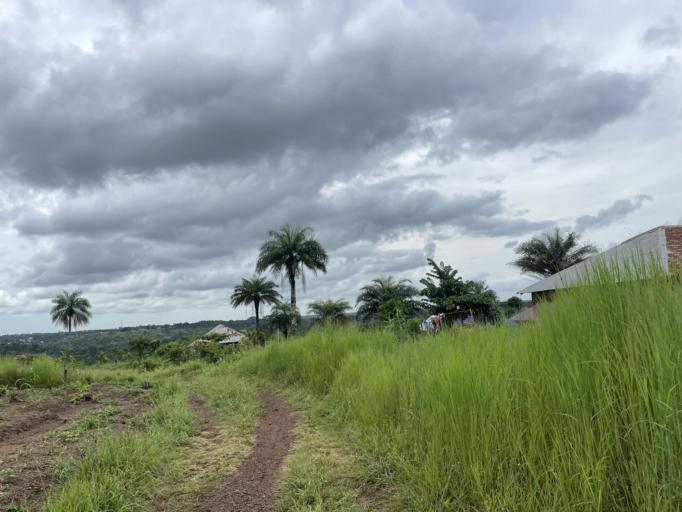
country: SL
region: Northern Province
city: Kambia
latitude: 9.1252
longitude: -12.9066
